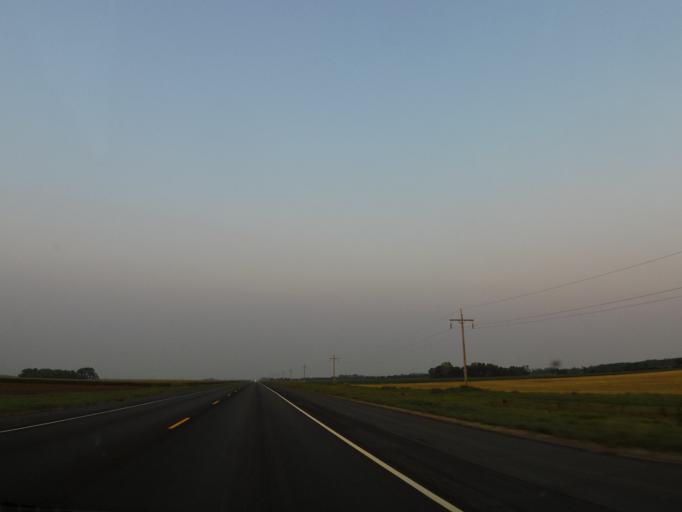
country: US
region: North Dakota
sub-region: Walsh County
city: Park River
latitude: 48.4127
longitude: -97.5930
